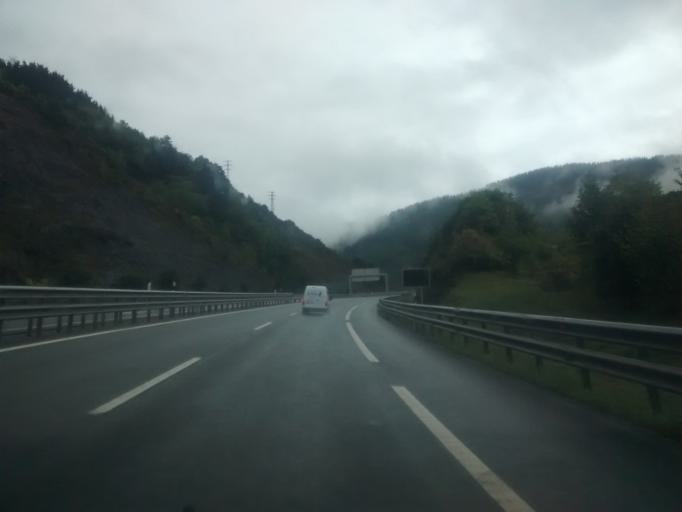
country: ES
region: Basque Country
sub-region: Provincia de Guipuzcoa
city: Elgoibar
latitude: 43.1885
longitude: -2.4292
